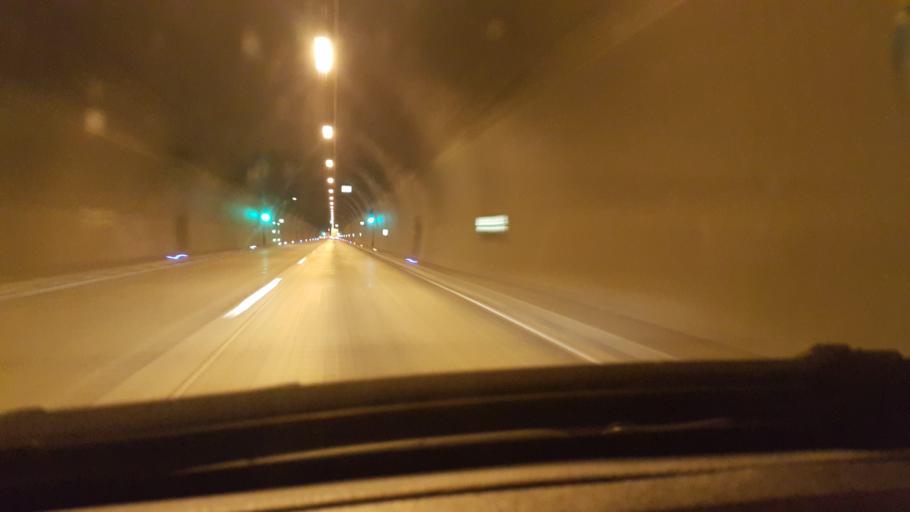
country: SI
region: Zagorje ob Savi
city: Izlake
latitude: 46.1865
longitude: 14.8753
